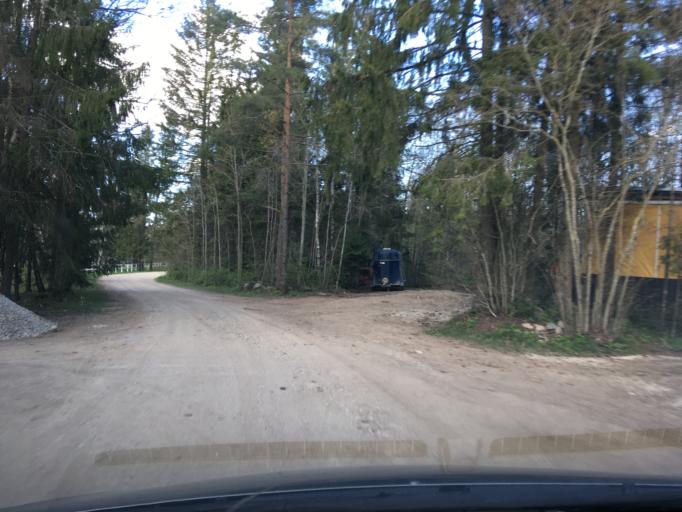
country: EE
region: Harju
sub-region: Raasiku vald
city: Raasiku
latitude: 59.2116
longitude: 25.1718
